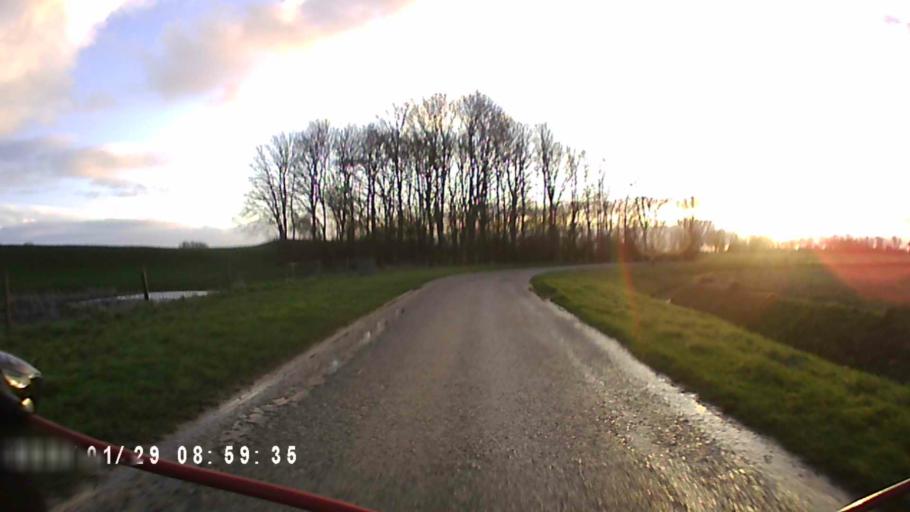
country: NL
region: Groningen
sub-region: Gemeente Winsum
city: Winsum
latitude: 53.3211
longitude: 6.4615
